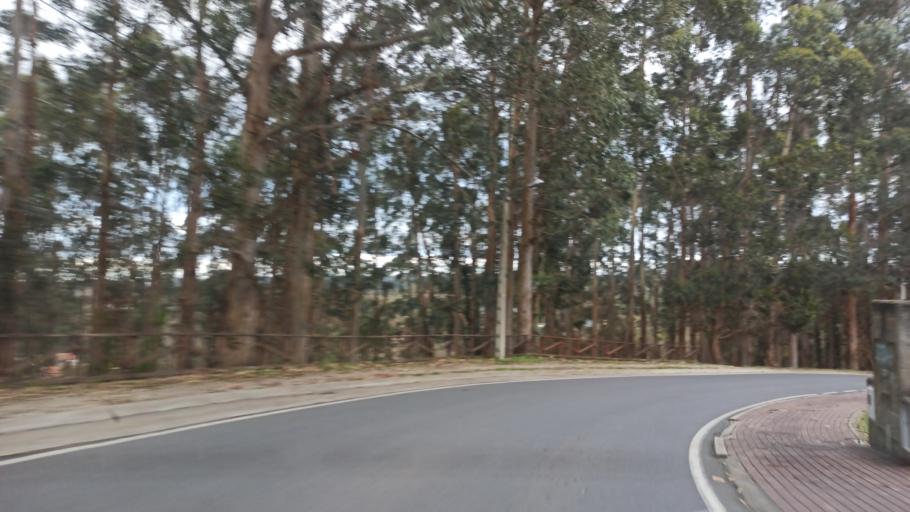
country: ES
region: Galicia
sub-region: Provincia da Coruna
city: Oleiros
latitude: 43.3348
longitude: -8.3537
